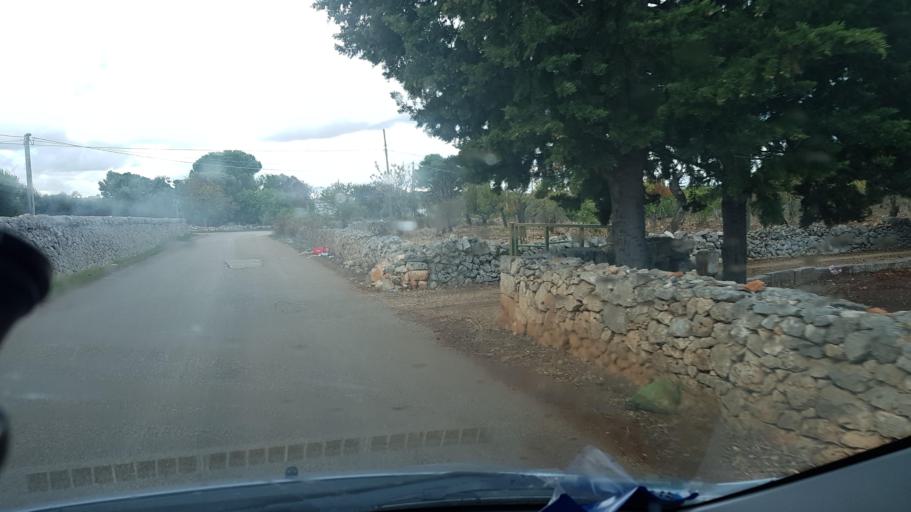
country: IT
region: Apulia
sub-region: Provincia di Brindisi
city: San Vito dei Normanni
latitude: 40.6526
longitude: 17.7222
